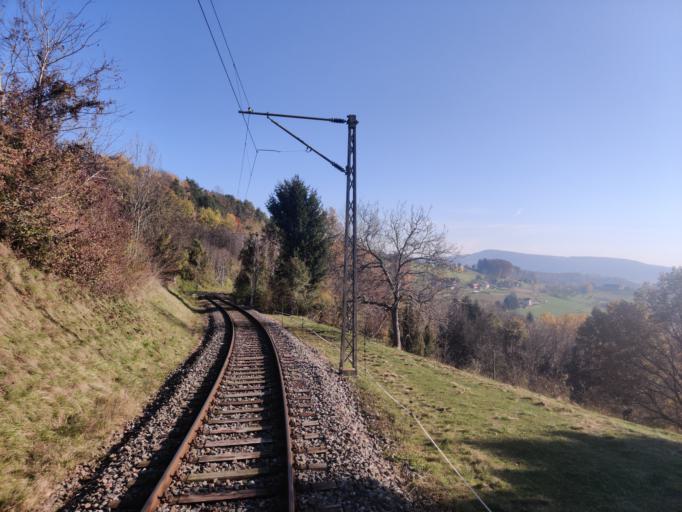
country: AT
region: Styria
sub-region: Politischer Bezirk Suedoststeiermark
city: Trautmannsdorf in Oststeiermark
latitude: 46.8880
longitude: 15.8764
